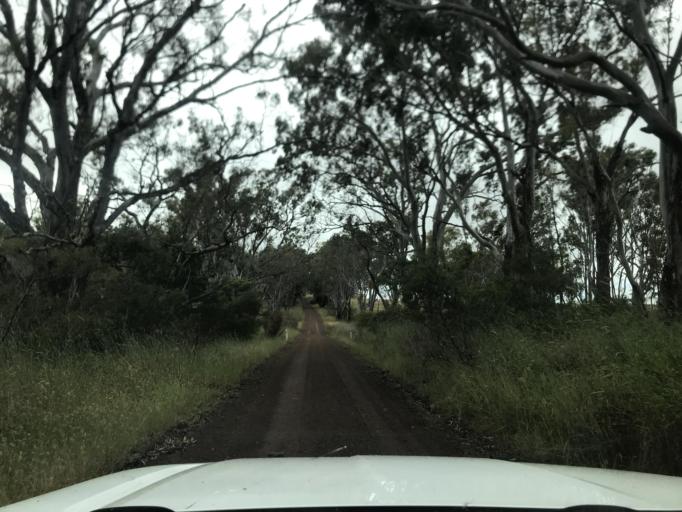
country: AU
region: South Australia
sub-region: Wattle Range
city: Penola
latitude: -37.2345
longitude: 141.4369
